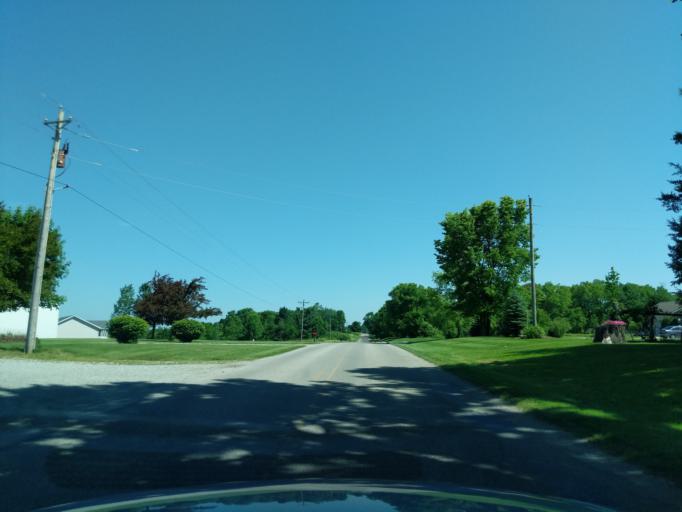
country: US
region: Indiana
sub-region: Huntington County
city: Huntington
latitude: 40.8379
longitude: -85.5087
